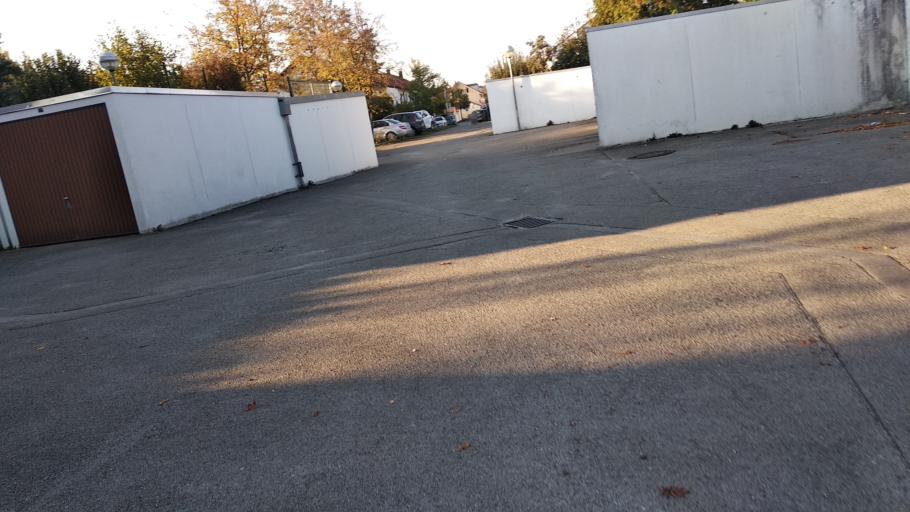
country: DE
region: Bavaria
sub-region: Upper Bavaria
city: Aschheim
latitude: 48.1691
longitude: 11.7113
